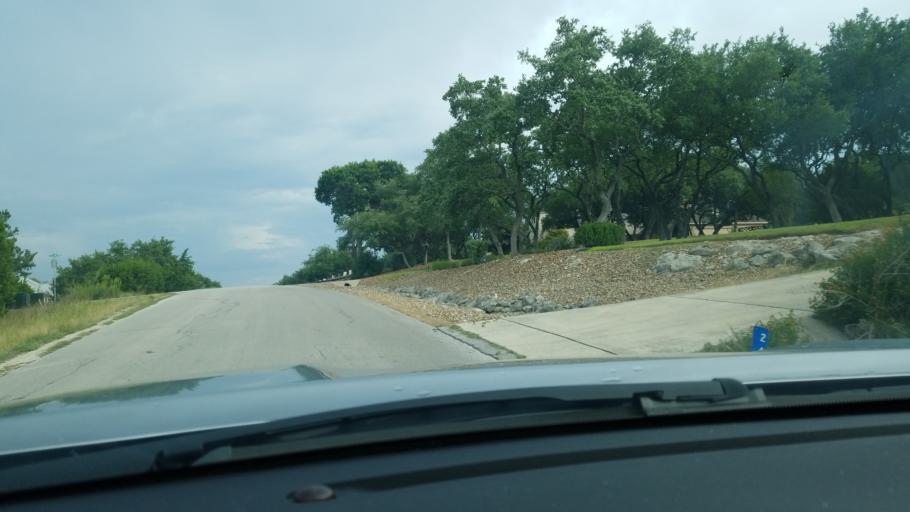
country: US
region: Texas
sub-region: Comal County
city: Bulverde
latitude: 29.8360
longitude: -98.4040
